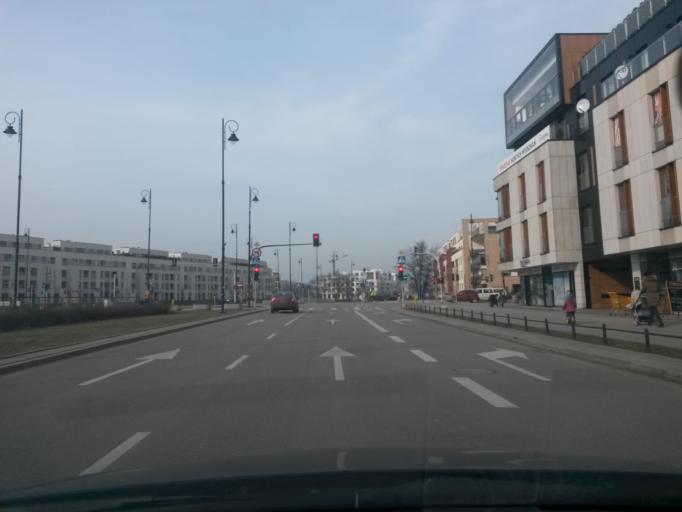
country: PL
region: Masovian Voivodeship
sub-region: Warszawa
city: Wilanow
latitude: 52.1598
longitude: 21.0731
